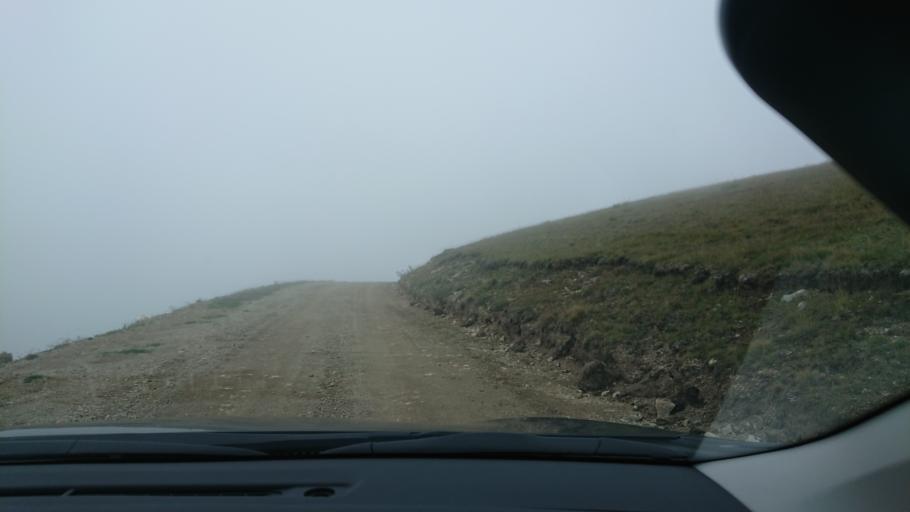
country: TR
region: Gumushane
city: Kurtun
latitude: 40.6254
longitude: 38.9935
